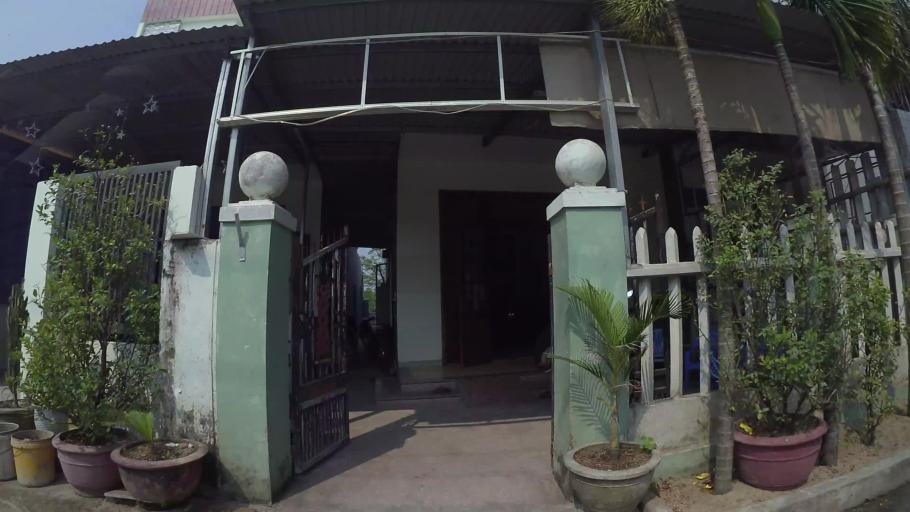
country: VN
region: Da Nang
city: Ngu Hanh Son
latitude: 15.9964
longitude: 108.2386
